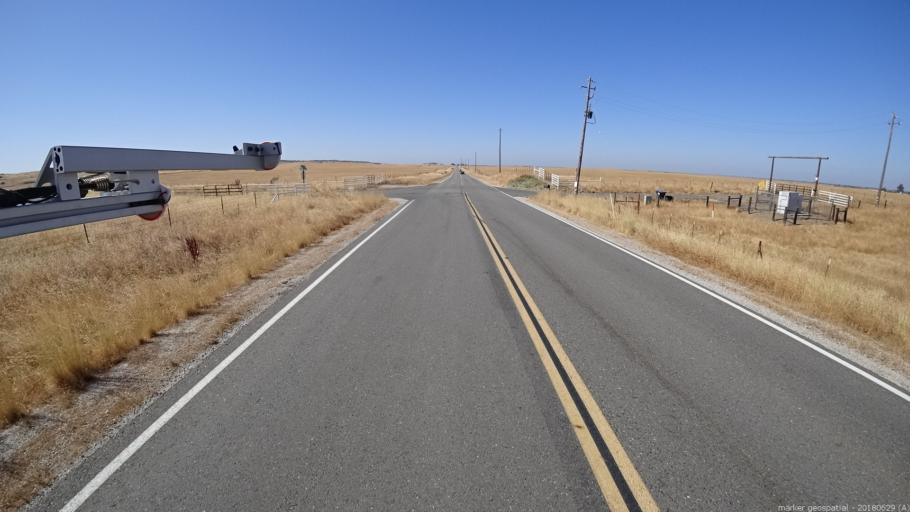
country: US
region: California
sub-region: Madera County
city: Bonadelle Ranchos-Madera Ranchos
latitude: 37.0396
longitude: -119.7937
